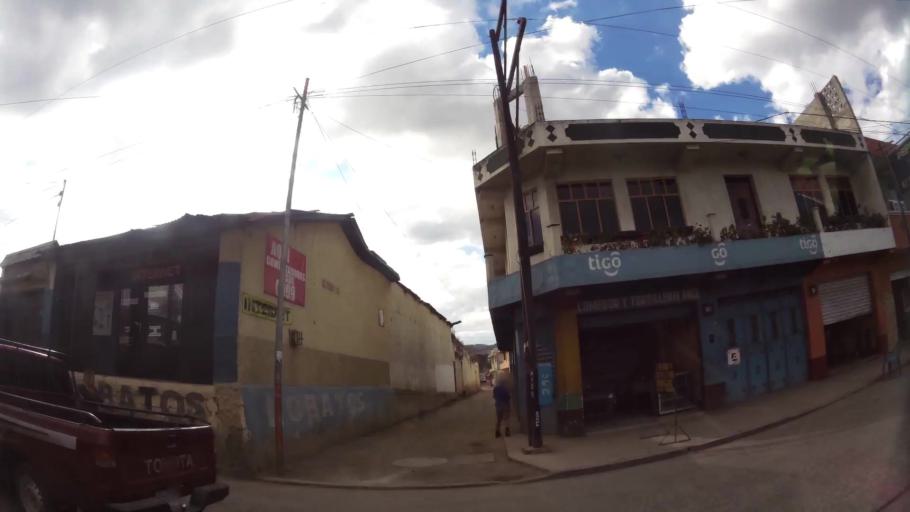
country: GT
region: Quetzaltenango
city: Quetzaltenango
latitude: 14.8379
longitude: -91.5357
